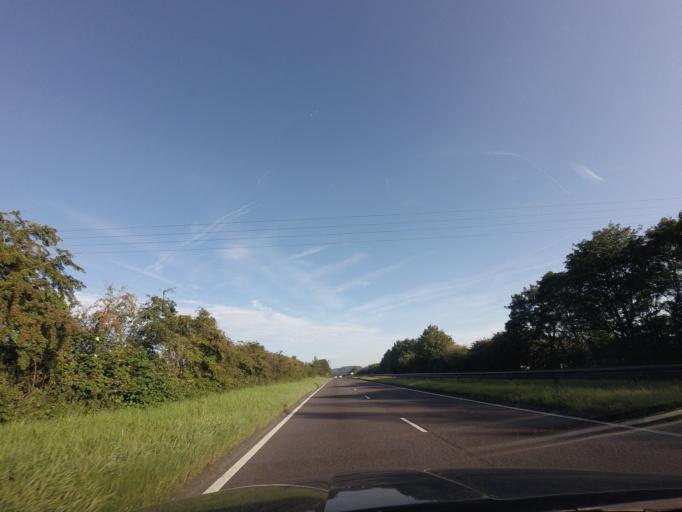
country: GB
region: England
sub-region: Derbyshire
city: Chesterfield
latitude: 53.2161
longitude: -1.3948
